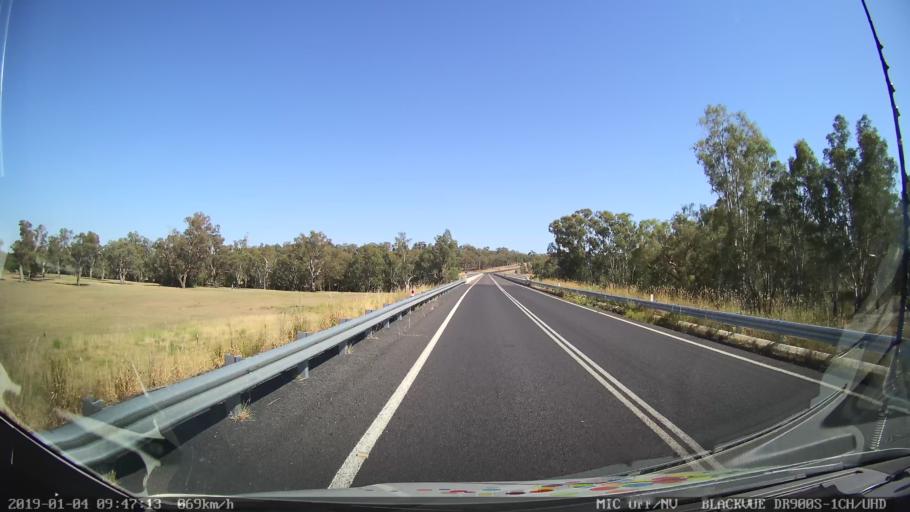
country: AU
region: New South Wales
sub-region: Cabonne
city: Canowindra
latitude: -33.6085
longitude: 148.4330
